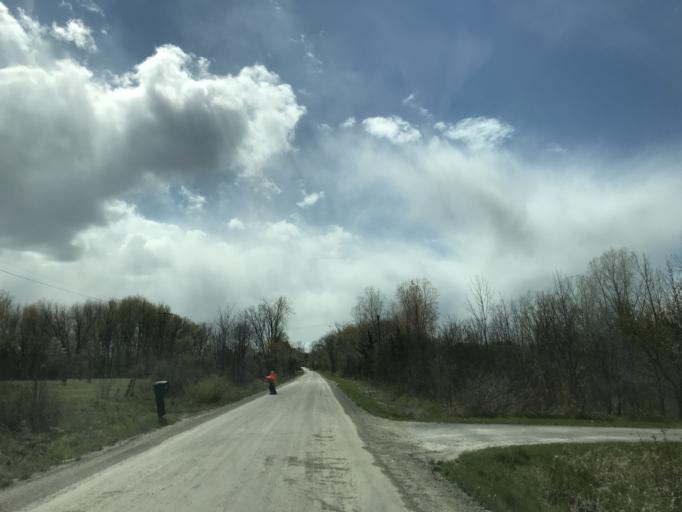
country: US
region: Michigan
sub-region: Oakland County
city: South Lyon
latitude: 42.3762
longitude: -83.6222
